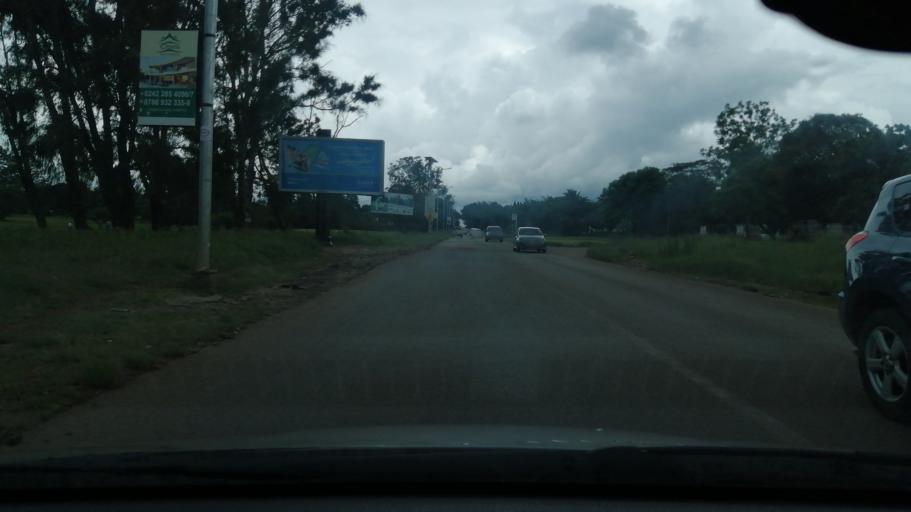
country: ZW
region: Harare
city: Harare
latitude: -17.8005
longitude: 31.0741
